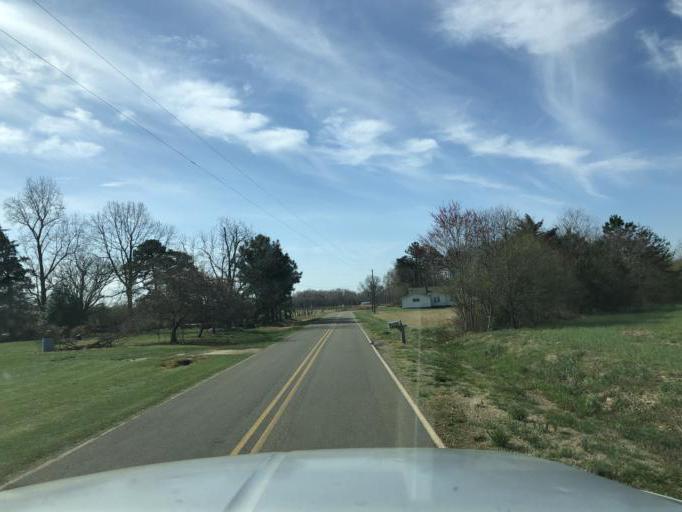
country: US
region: North Carolina
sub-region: Cleveland County
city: Shelby
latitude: 35.4832
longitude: -81.6410
